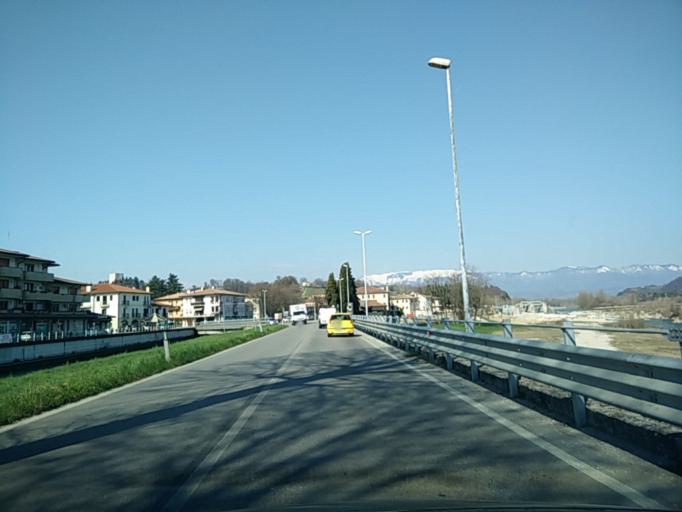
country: IT
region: Veneto
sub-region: Provincia di Treviso
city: Nervesa della Battaglia
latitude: 45.8251
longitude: 12.2130
